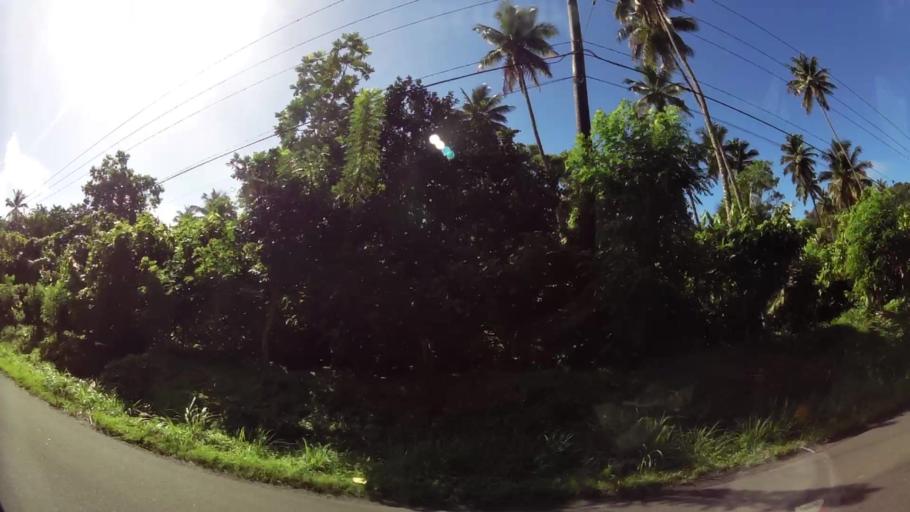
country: LC
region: Soufriere
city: Soufriere
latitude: 13.8216
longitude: -61.0458
